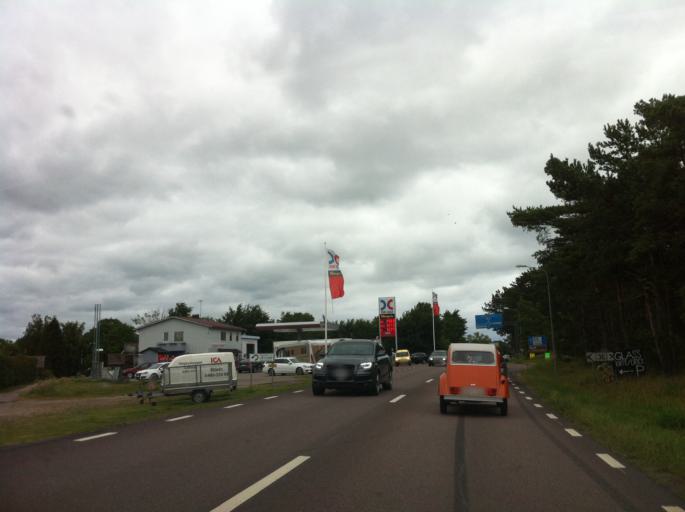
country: SE
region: Kalmar
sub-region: Borgholms Kommun
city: Borgholm
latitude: 57.1628
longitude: 17.0121
